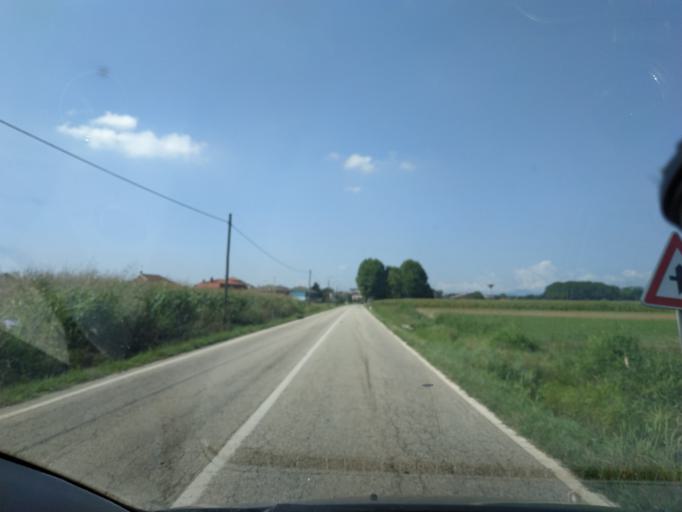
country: IT
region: Piedmont
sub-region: Provincia di Torino
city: San Benigno Canavese
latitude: 45.2327
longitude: 7.7924
